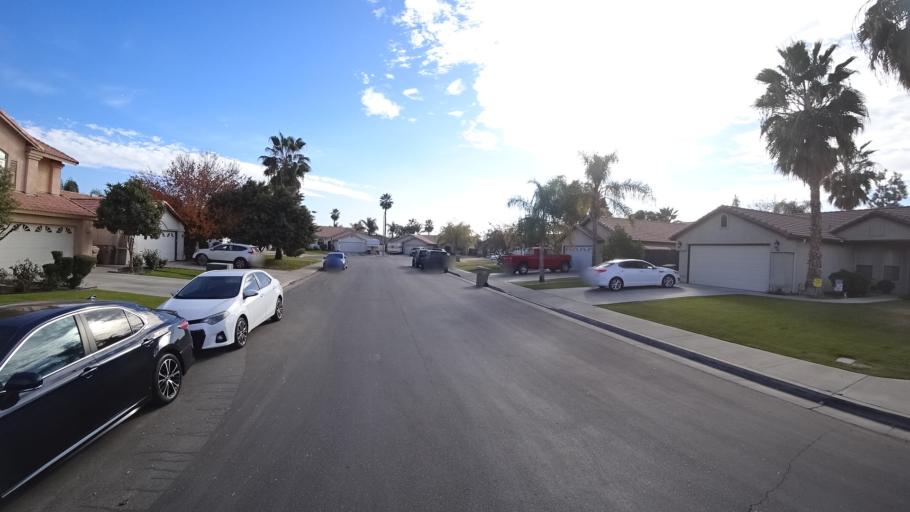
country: US
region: California
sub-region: Kern County
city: Greenacres
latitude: 35.4015
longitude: -119.1182
